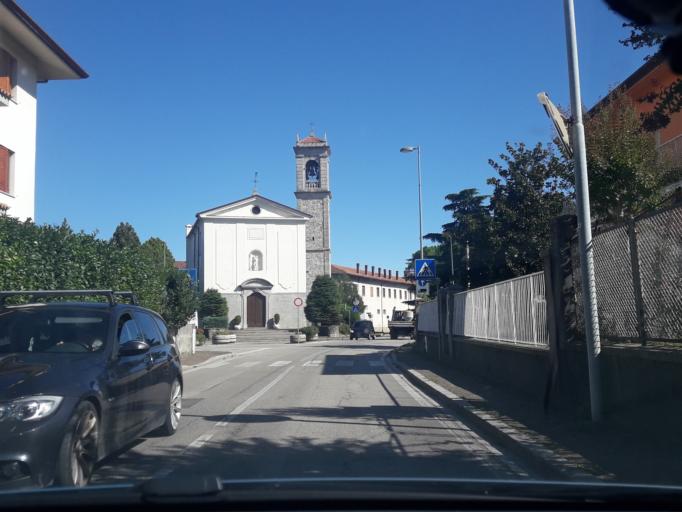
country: IT
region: Friuli Venezia Giulia
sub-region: Provincia di Udine
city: Tavagnacco
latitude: 46.1158
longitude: 13.2319
